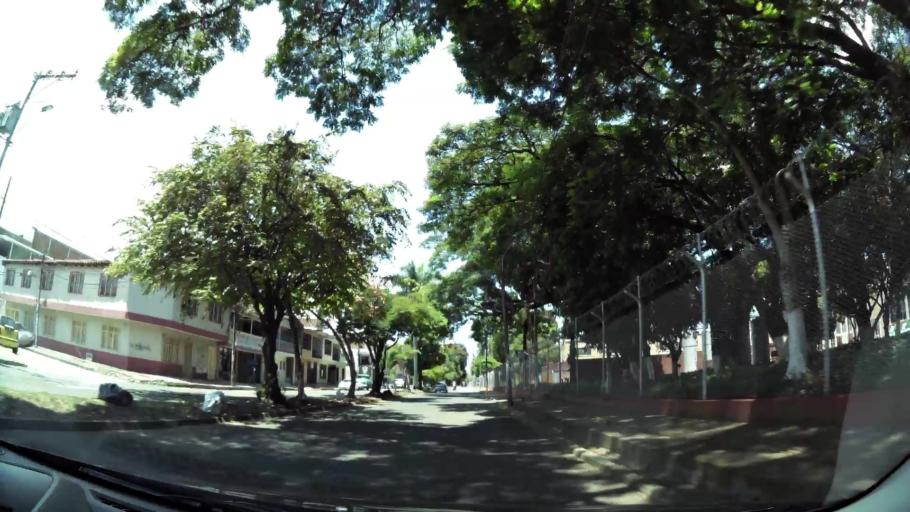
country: CO
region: Valle del Cauca
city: Cali
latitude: 3.4465
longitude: -76.4939
